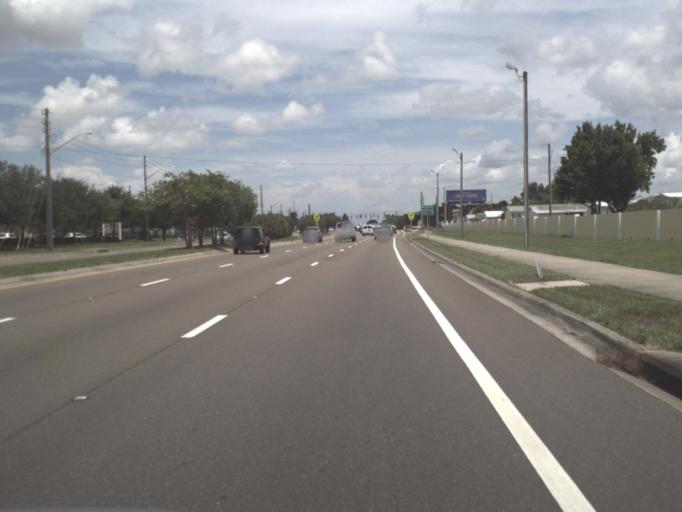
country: US
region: Florida
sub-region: Pinellas County
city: Safety Harbor
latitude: 28.0197
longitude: -82.7089
